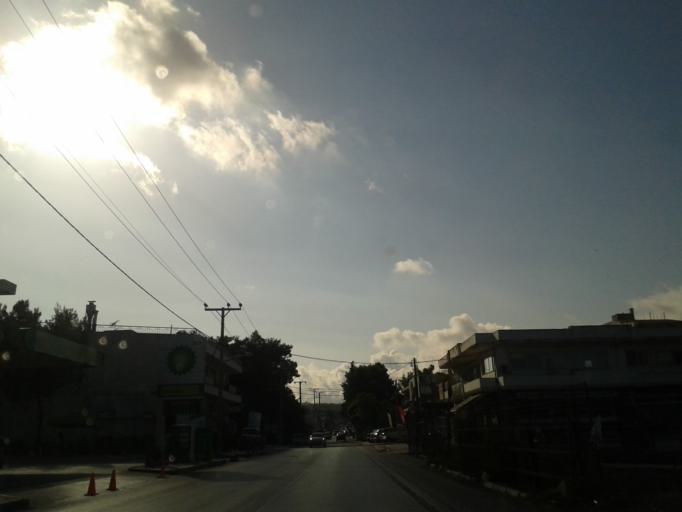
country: GR
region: Attica
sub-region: Nomarchia Anatolikis Attikis
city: Anoixi
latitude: 38.1369
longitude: 23.8559
